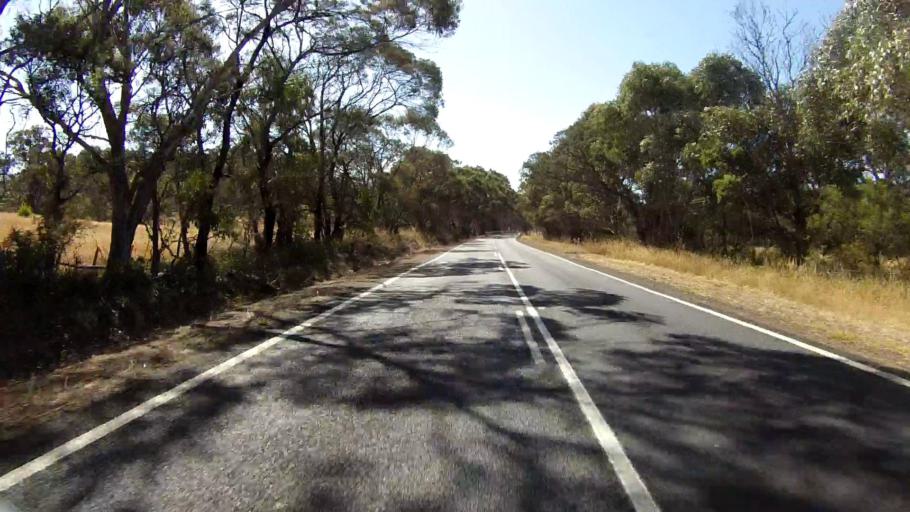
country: AU
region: Tasmania
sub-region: Sorell
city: Sorell
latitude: -42.4149
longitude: 147.9346
